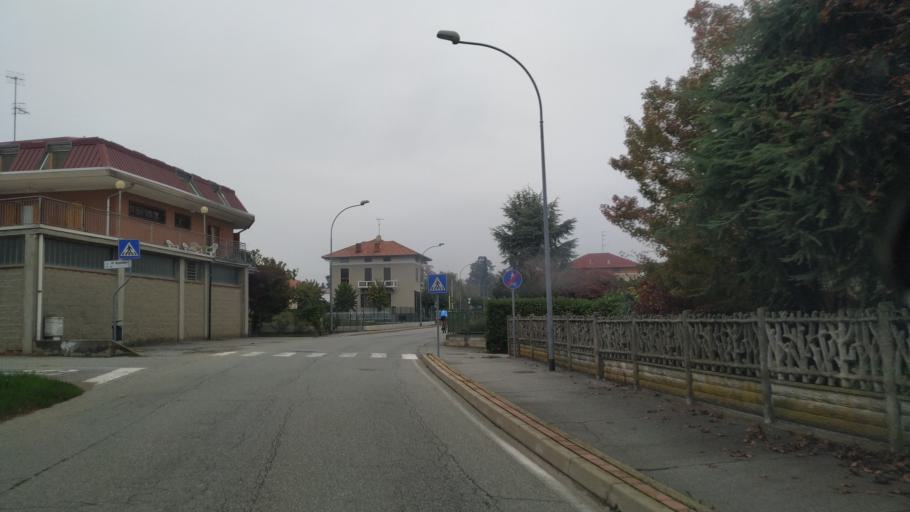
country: IT
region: Piedmont
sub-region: Provincia di Biella
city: Lessona
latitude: 45.5807
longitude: 8.1990
